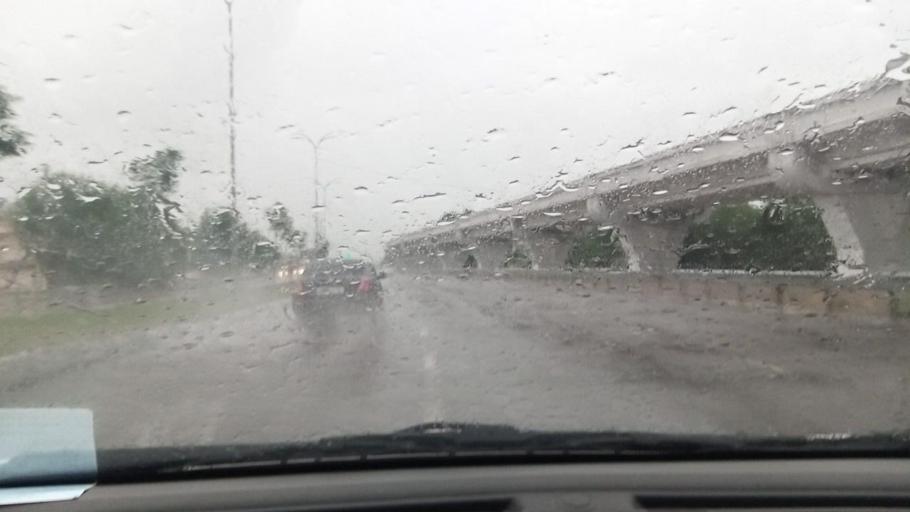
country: UZ
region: Toshkent Shahri
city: Bektemir
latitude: 41.2706
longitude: 69.3633
